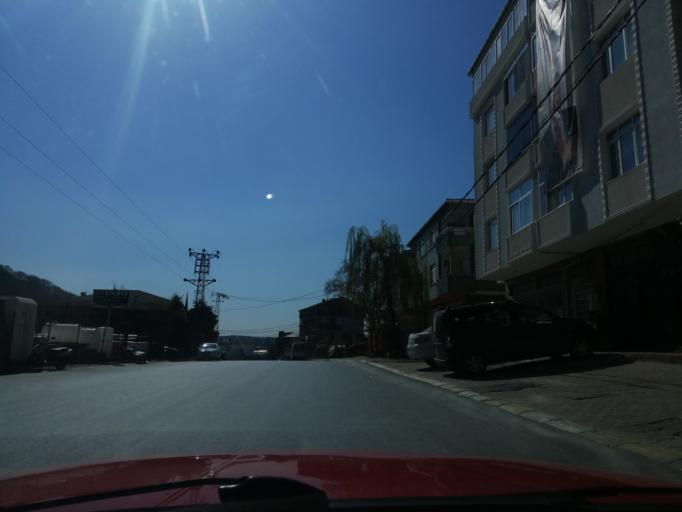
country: TR
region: Istanbul
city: Mahmut Sevket Pasa
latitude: 41.0981
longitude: 29.1511
